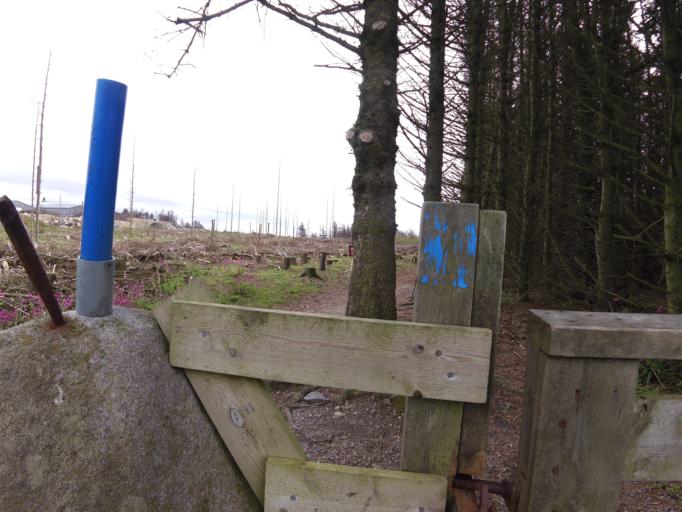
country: NO
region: Rogaland
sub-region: Ha
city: Naerbo
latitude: 58.6315
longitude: 5.5934
